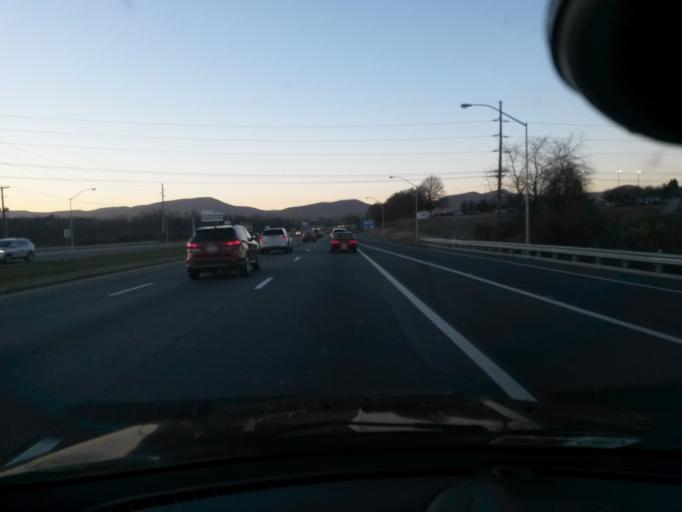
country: US
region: Virginia
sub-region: City of Roanoke
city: Roanoke
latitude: 37.2999
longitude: -79.9622
